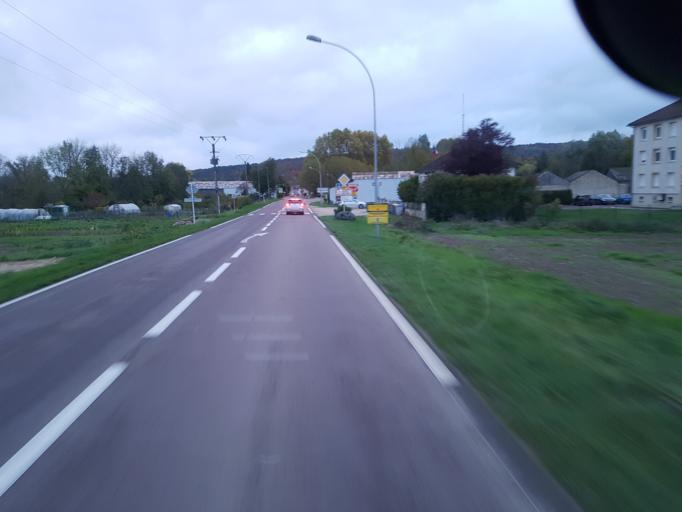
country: FR
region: Champagne-Ardenne
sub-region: Departement de l'Aube
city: Mussy-sur-Seine
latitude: 47.9728
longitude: 4.5006
